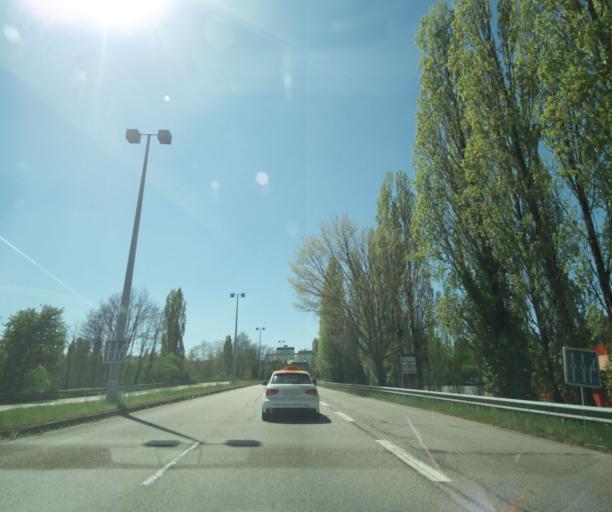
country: FR
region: Limousin
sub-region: Departement de la Haute-Vienne
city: Limoges
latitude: 45.8355
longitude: 1.2778
